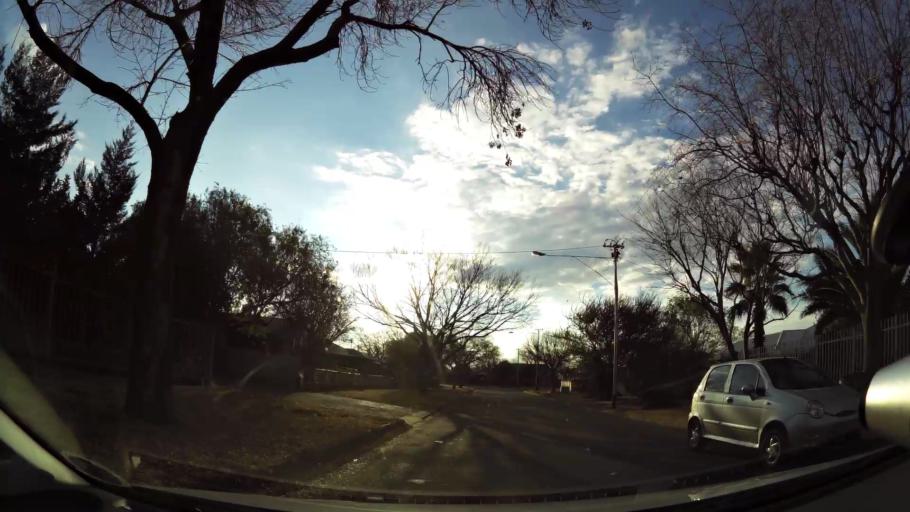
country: ZA
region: Orange Free State
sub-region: Mangaung Metropolitan Municipality
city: Bloemfontein
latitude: -29.1394
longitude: 26.1957
